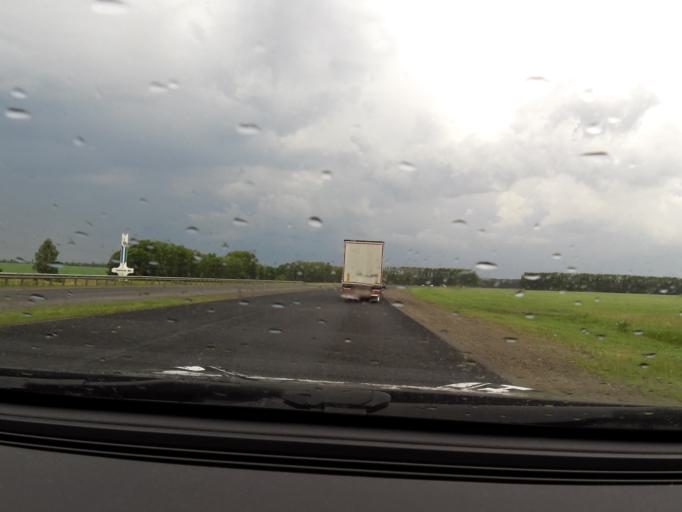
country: RU
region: Bashkortostan
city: Asanovo
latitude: 54.9206
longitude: 55.5819
